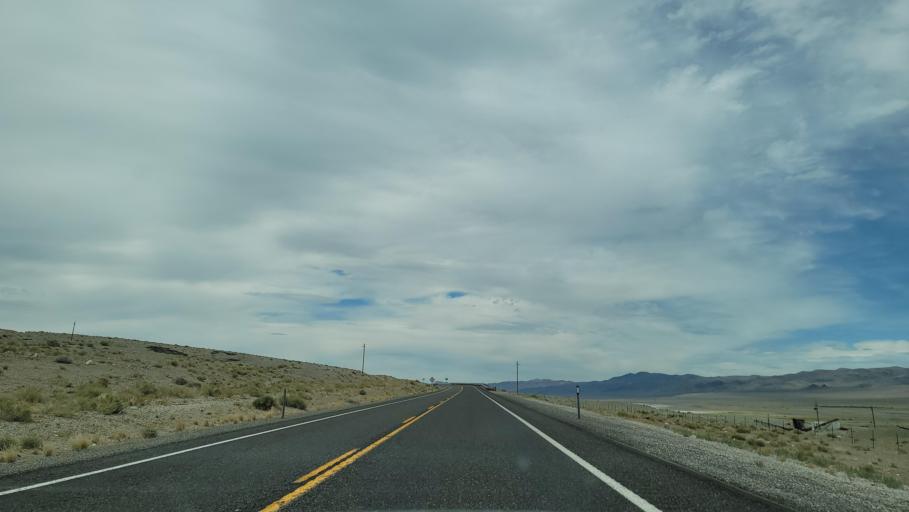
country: US
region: Nevada
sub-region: Mineral County
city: Hawthorne
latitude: 38.5927
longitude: -118.7080
